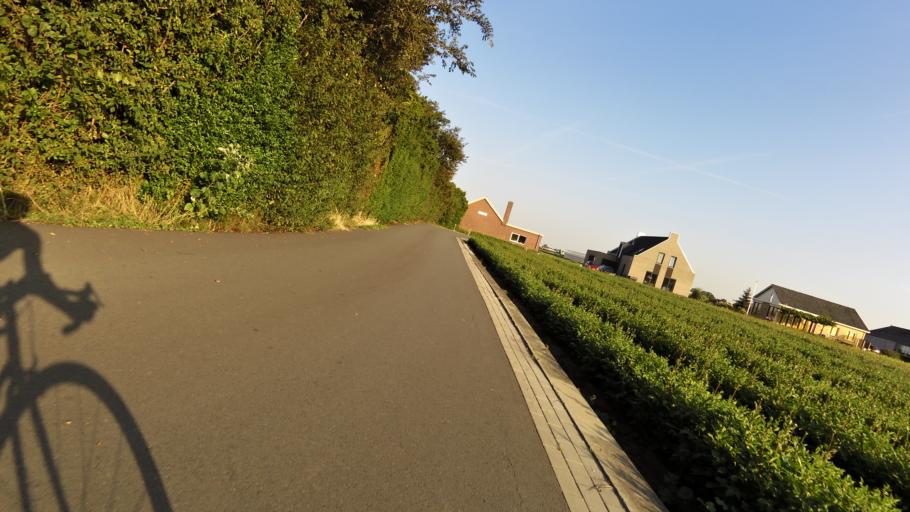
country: NL
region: South Holland
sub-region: Gemeente Noordwijkerhout
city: Noordwijkerhout
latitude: 52.2468
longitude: 4.4841
